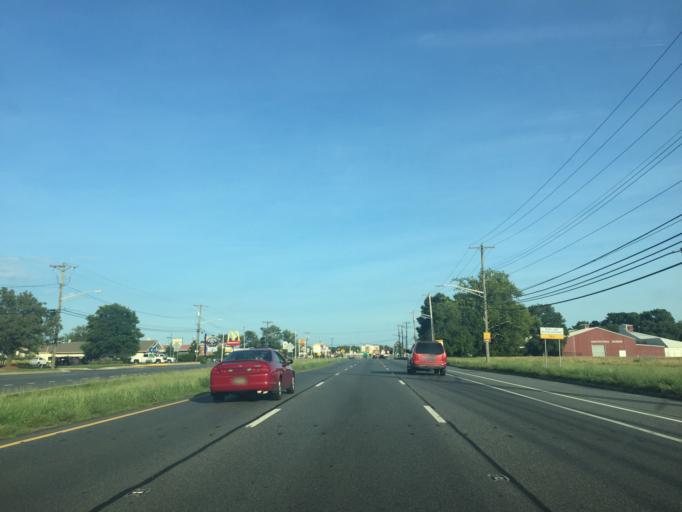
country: US
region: Delaware
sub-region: Kent County
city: Dover
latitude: 39.1839
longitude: -75.5335
